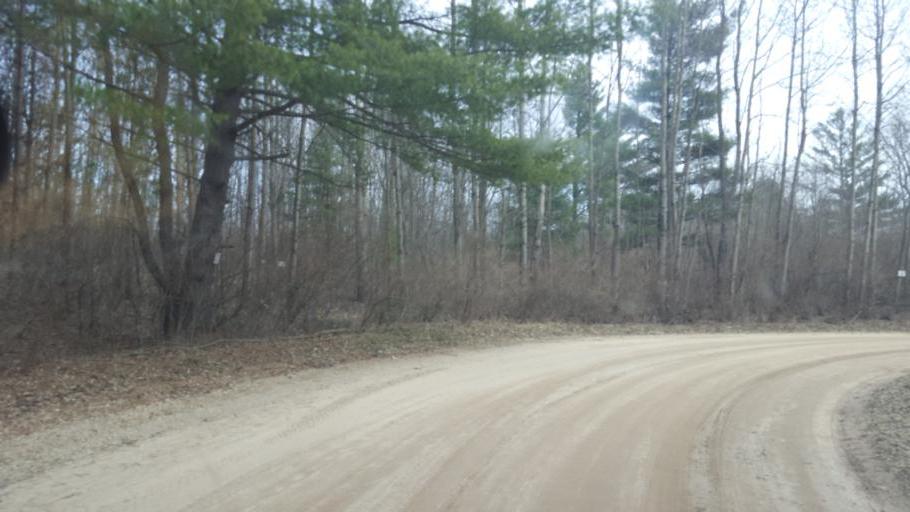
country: US
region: Michigan
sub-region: Isabella County
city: Lake Isabella
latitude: 43.6829
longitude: -85.1369
